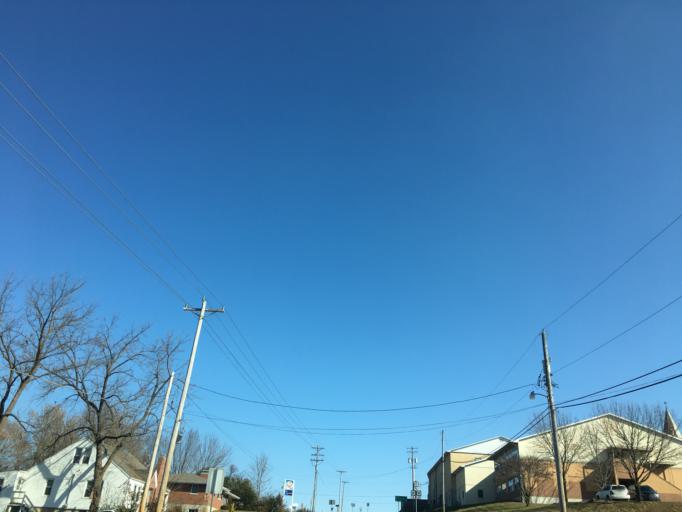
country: US
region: Missouri
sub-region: Cole County
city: Wardsville
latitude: 38.4883
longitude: -92.1779
